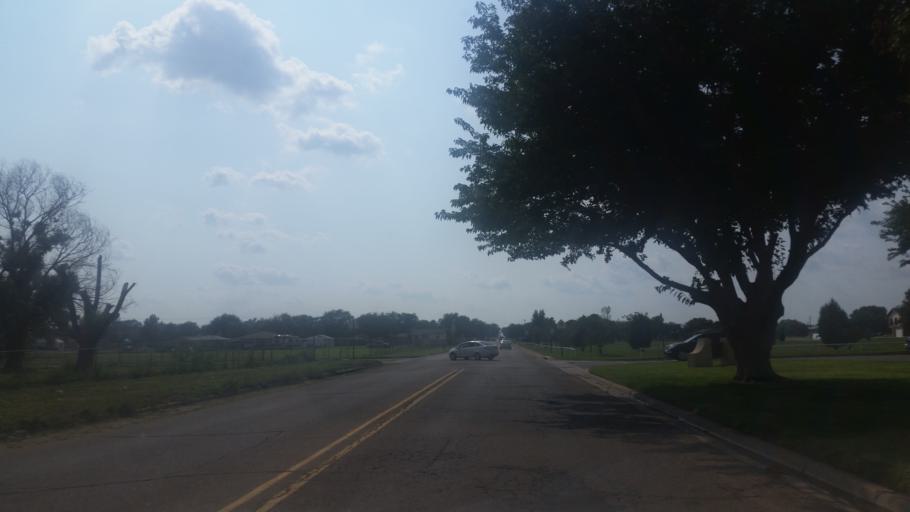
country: US
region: New Mexico
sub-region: Curry County
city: Clovis
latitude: 34.4121
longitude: -103.1908
